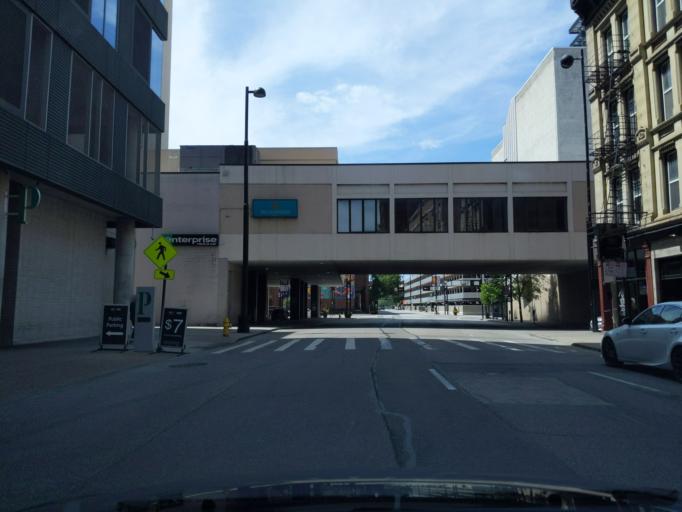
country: US
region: Kentucky
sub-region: Kenton County
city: Covington
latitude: 39.1021
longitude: -84.5154
